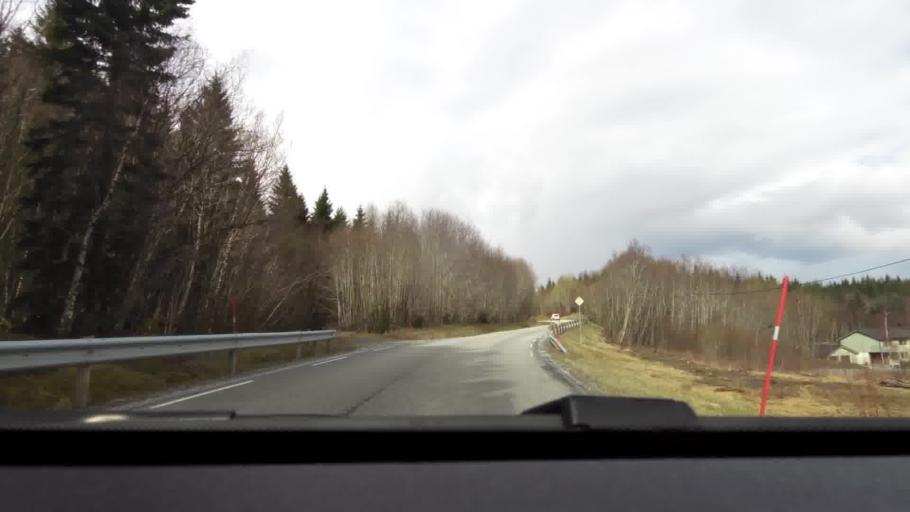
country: NO
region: More og Romsdal
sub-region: Averoy
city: Bruhagen
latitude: 63.1044
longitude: 7.6280
